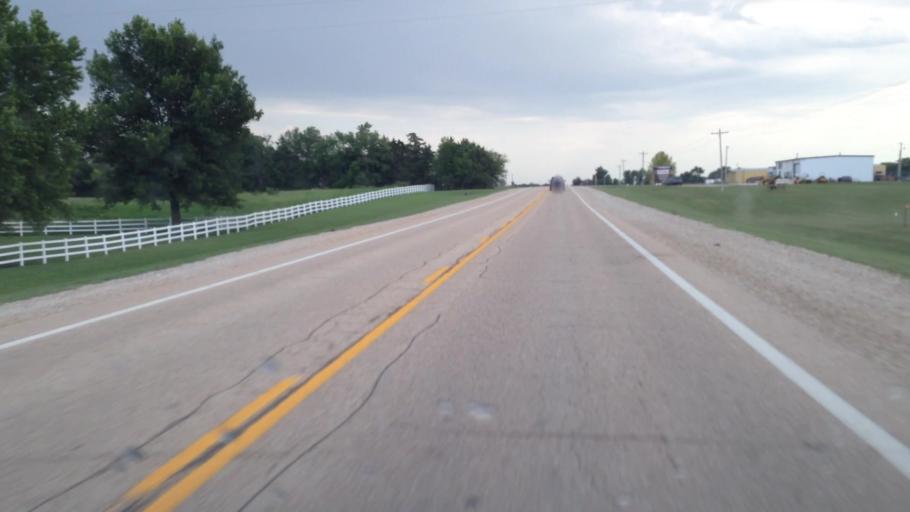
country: US
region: Kansas
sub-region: Coffey County
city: Burlington
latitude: 38.1806
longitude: -95.7388
